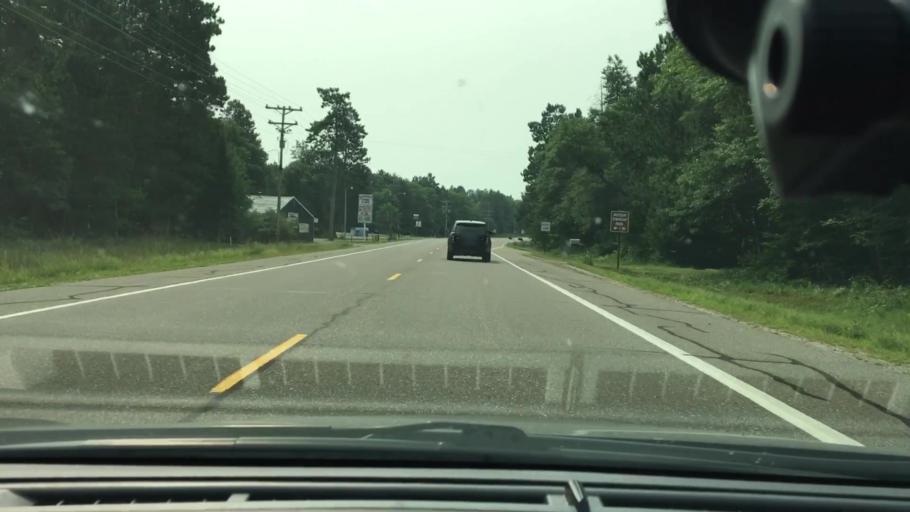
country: US
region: Minnesota
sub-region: Crow Wing County
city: Cross Lake
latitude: 46.5748
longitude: -94.1304
